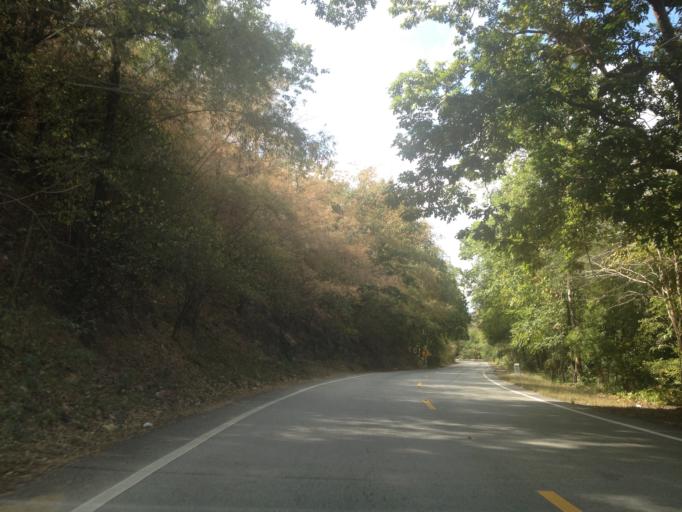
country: TH
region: Chiang Mai
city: Hot
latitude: 18.2268
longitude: 98.5032
